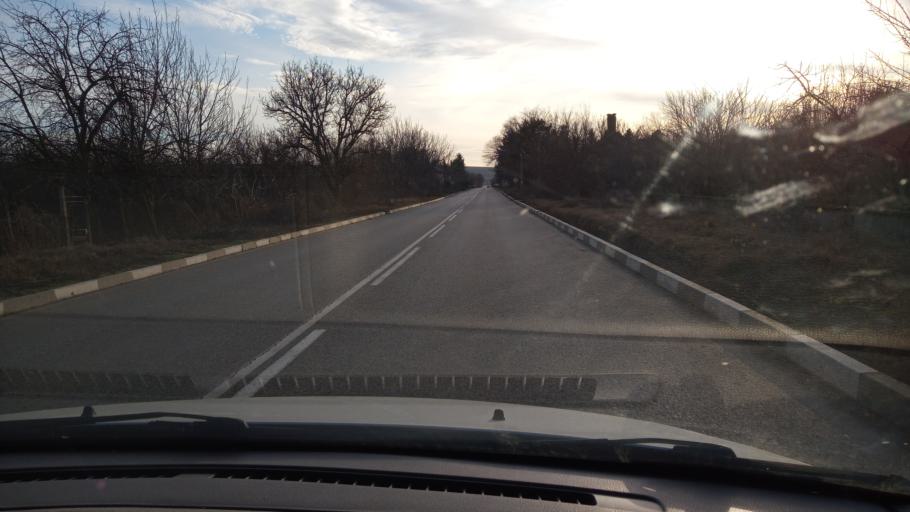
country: BG
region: Pleven
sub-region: Obshtina Pleven
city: Slavyanovo
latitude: 43.5563
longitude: 24.8665
